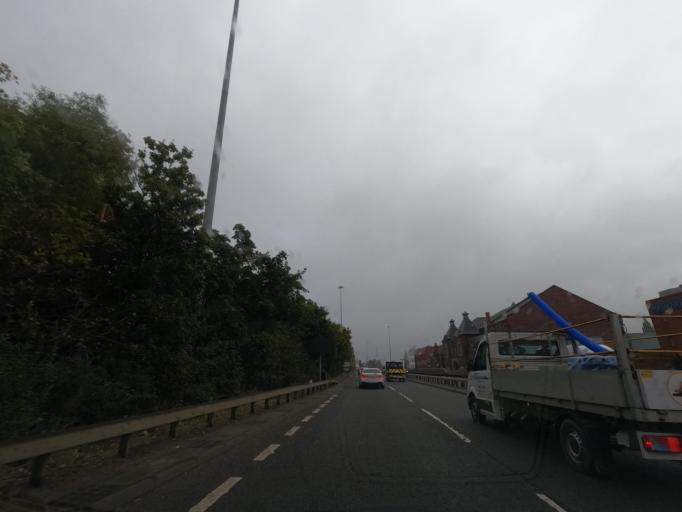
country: GB
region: England
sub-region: Middlesbrough
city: Middlesbrough
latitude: 54.5785
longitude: -1.2389
